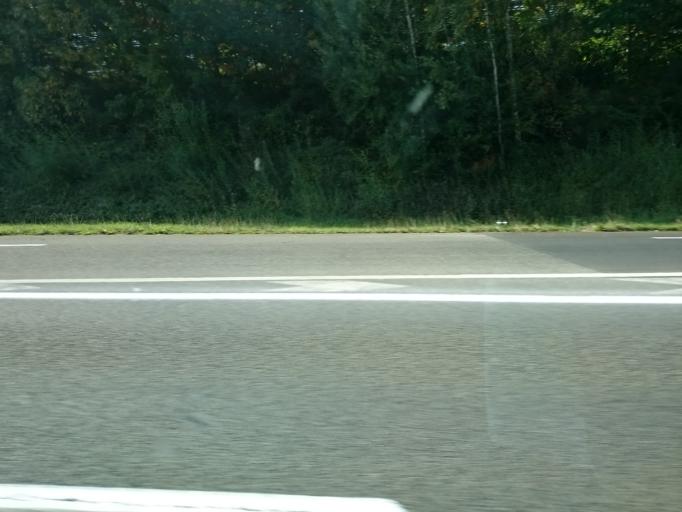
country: FR
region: Pays de la Loire
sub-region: Departement de la Loire-Atlantique
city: Orvault
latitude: 47.2582
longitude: -1.6213
